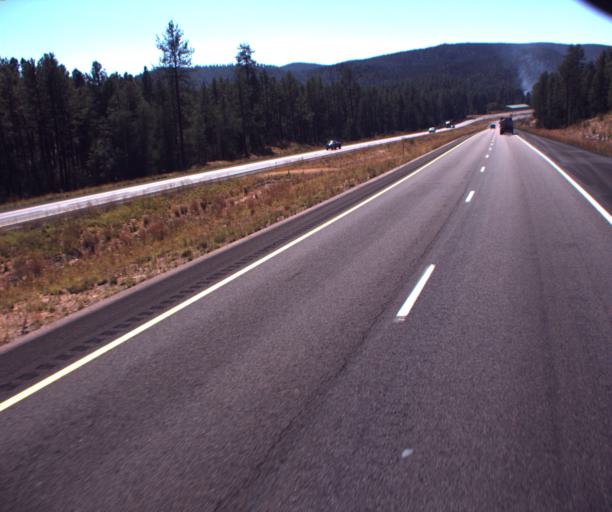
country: US
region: Arizona
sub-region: Gila County
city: Star Valley
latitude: 34.2883
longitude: -111.1404
